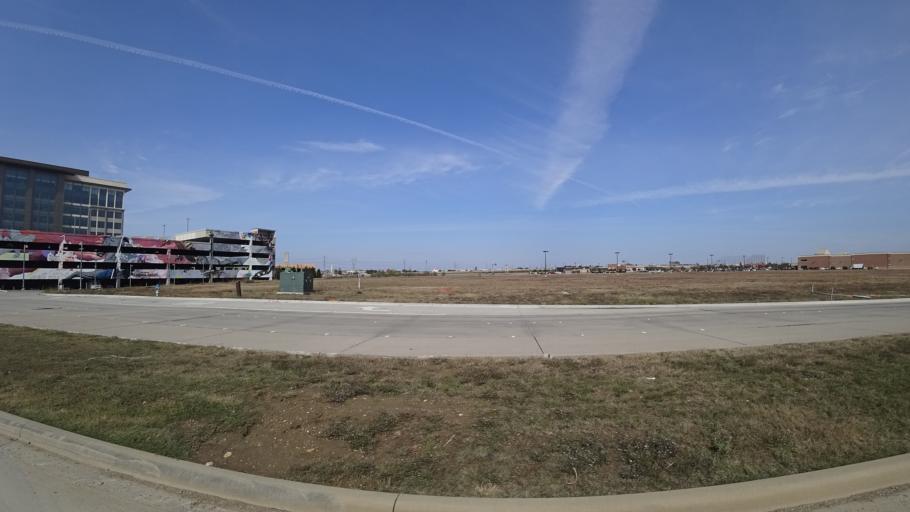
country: US
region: Texas
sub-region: Denton County
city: The Colony
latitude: 33.0604
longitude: -96.8921
